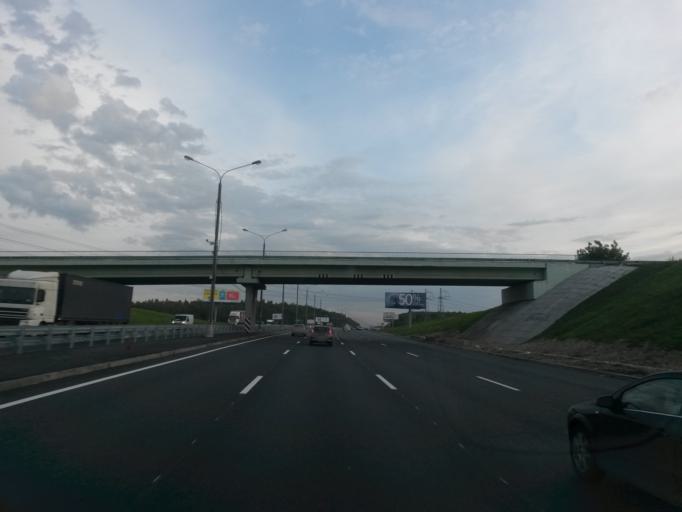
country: RU
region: Moscow
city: Annino
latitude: 55.5605
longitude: 37.6048
